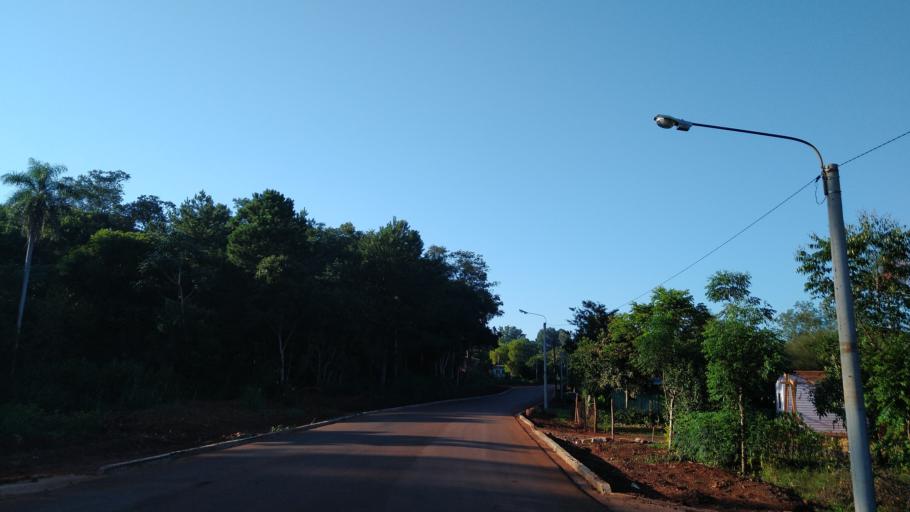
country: AR
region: Misiones
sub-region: Departamento de Montecarlo
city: Montecarlo
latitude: -26.5618
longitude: -54.7693
